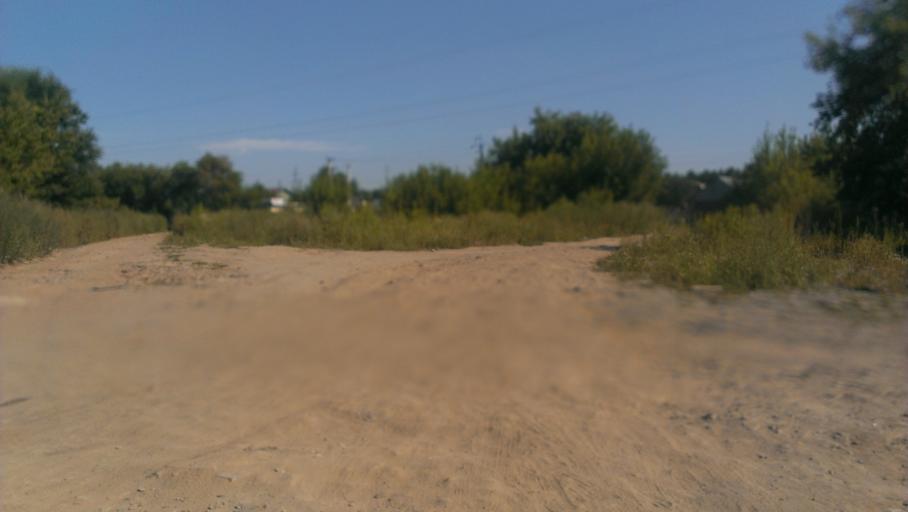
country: RU
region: Altai Krai
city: Novosilikatnyy
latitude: 53.3245
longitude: 83.6846
